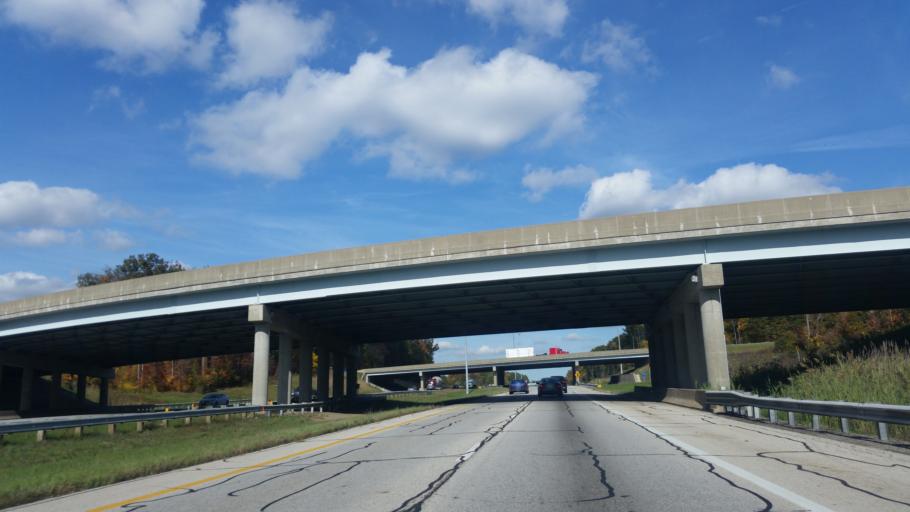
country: US
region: Ohio
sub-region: Summit County
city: Richfield
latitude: 41.2733
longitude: -81.6362
